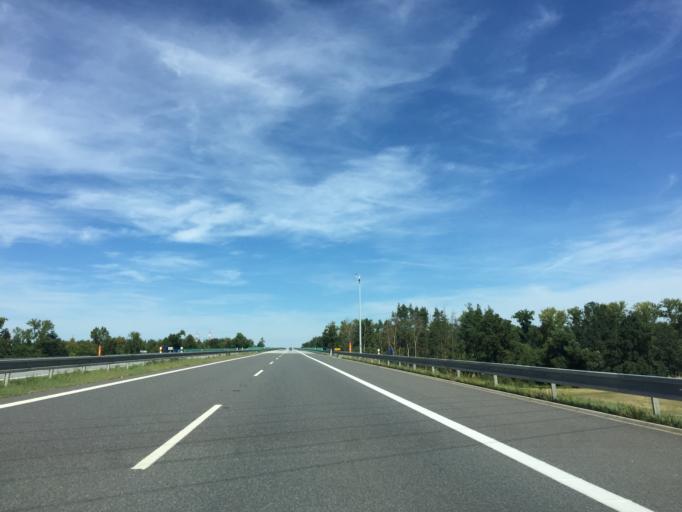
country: CZ
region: Jihocesky
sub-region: Okres Tabor
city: Veseli nad Luznici
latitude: 49.2062
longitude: 14.7093
